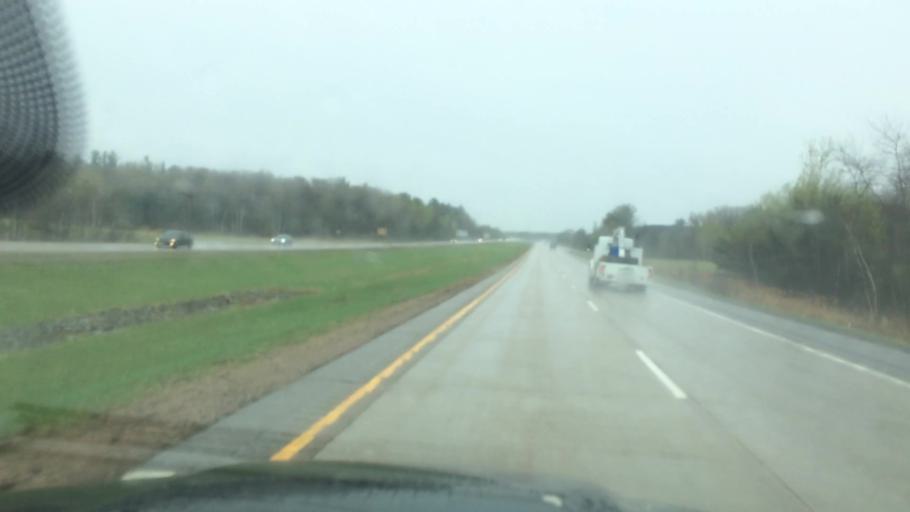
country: US
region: Wisconsin
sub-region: Marathon County
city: Mosinee
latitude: 44.6752
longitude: -89.6422
